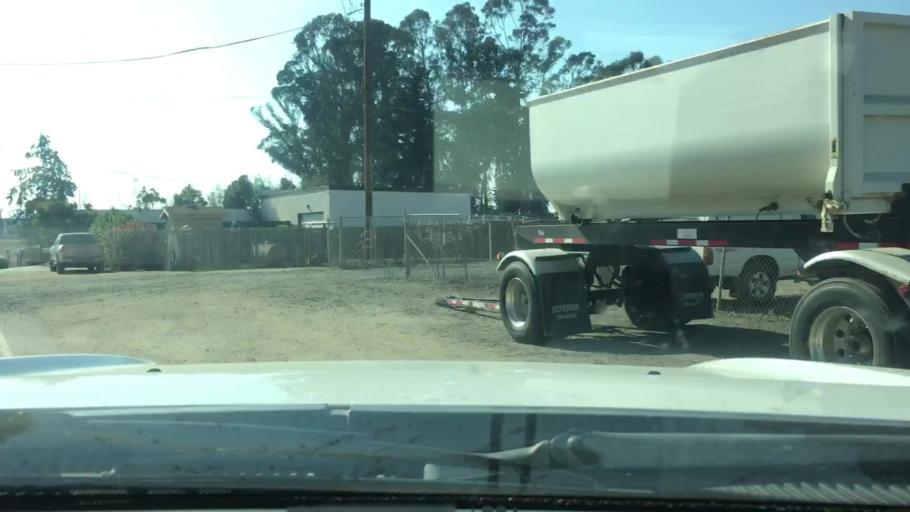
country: US
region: California
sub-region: San Luis Obispo County
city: Los Osos
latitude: 35.3128
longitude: -120.8294
